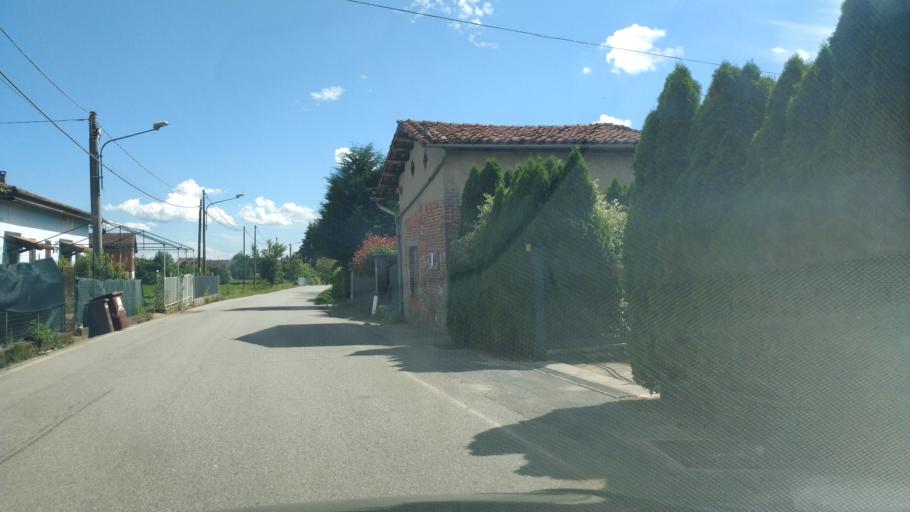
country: IT
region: Piedmont
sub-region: Provincia di Torino
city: Castellamonte
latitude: 45.3973
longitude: 7.7251
